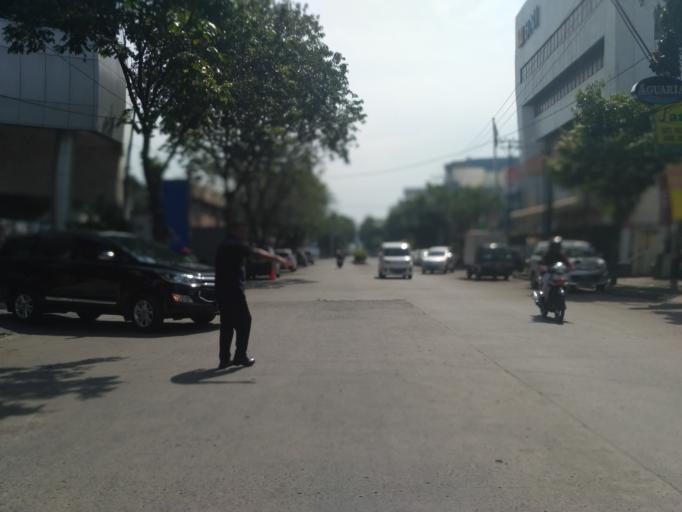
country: ID
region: Central Java
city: Semarang
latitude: -6.9684
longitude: 110.4310
